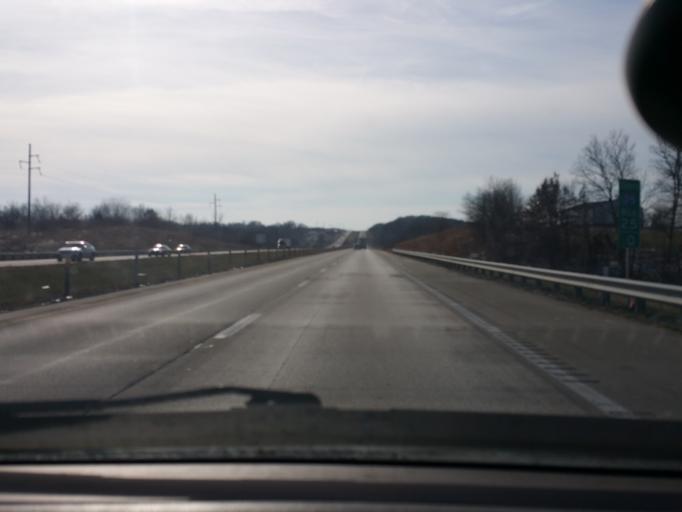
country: US
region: Missouri
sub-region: Clay County
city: Kearney
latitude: 39.3528
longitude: -94.3806
